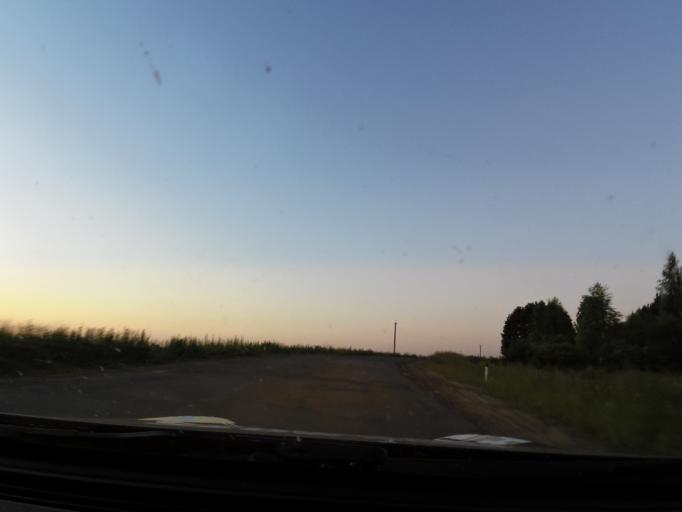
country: RU
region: Kostroma
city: Buy
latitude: 58.4796
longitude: 41.4424
